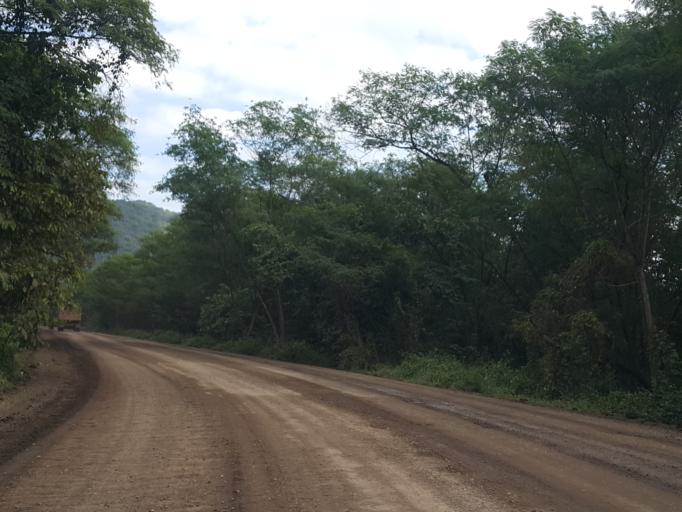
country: TH
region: Lampang
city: Mae Mo
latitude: 18.3137
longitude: 99.7471
